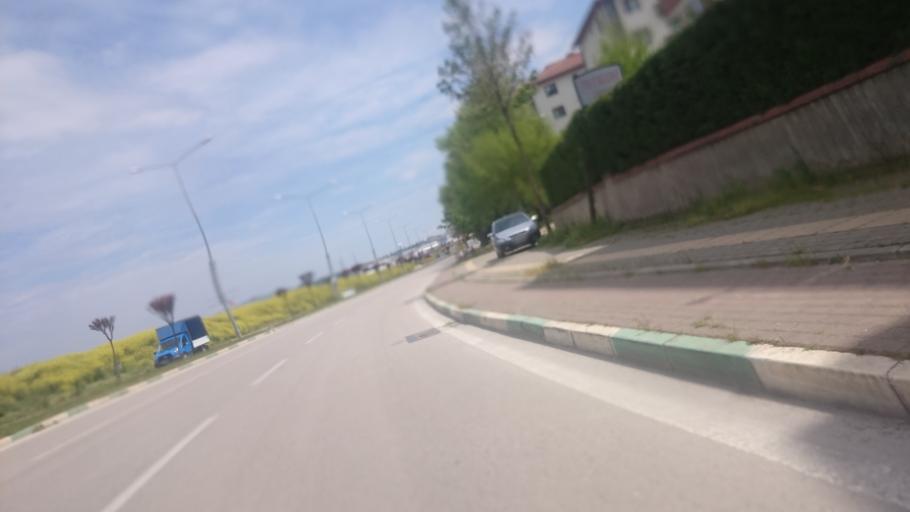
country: TR
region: Bursa
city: Niluefer
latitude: 40.2329
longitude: 28.9169
